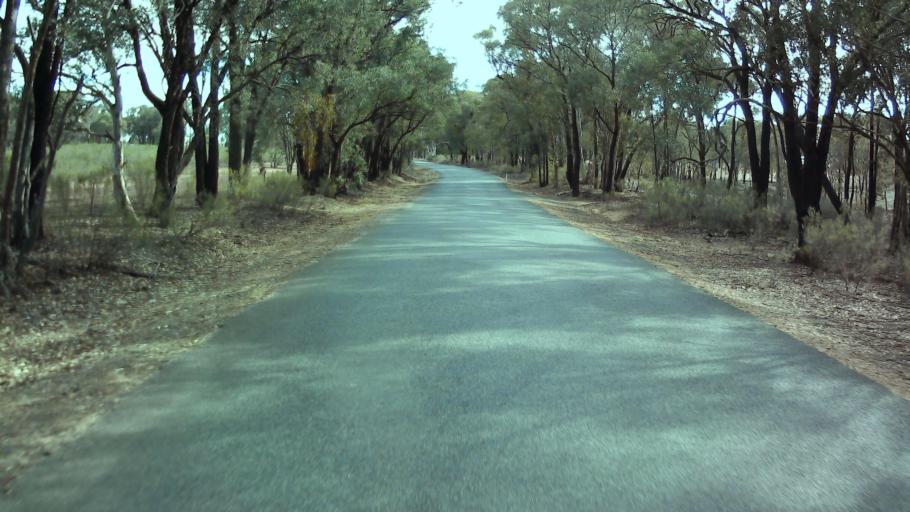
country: AU
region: New South Wales
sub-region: Weddin
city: Grenfell
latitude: -33.8842
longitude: 148.1986
